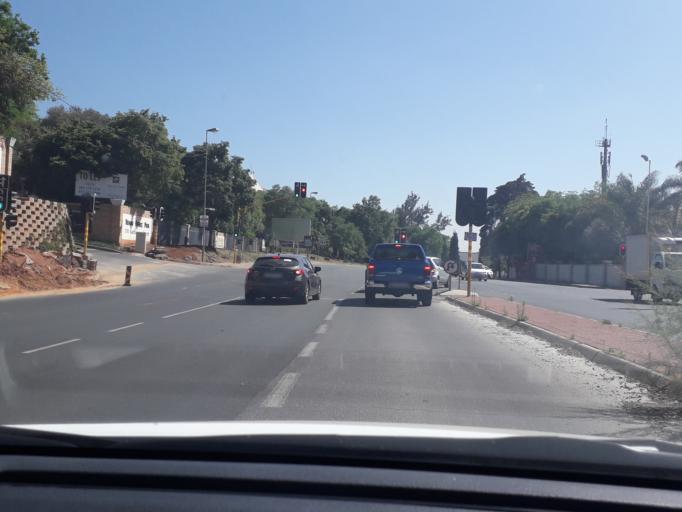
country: ZA
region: Gauteng
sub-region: City of Johannesburg Metropolitan Municipality
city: Modderfontein
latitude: -26.1019
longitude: 28.0730
